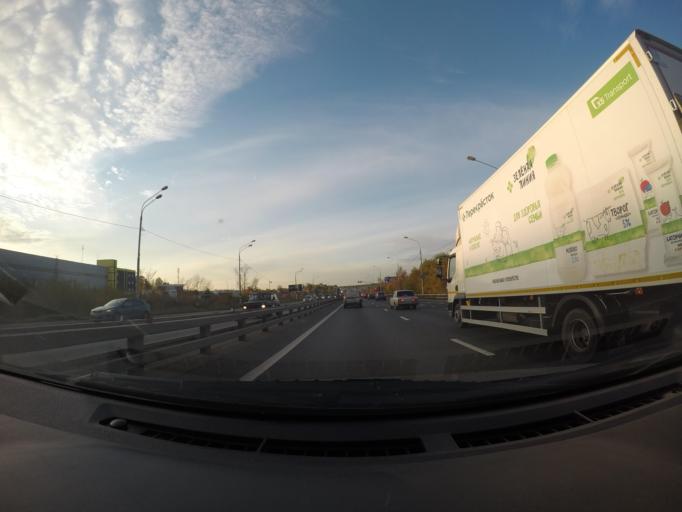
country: RU
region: Moskovskaya
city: Skhodnya
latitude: 55.9697
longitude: 37.3220
